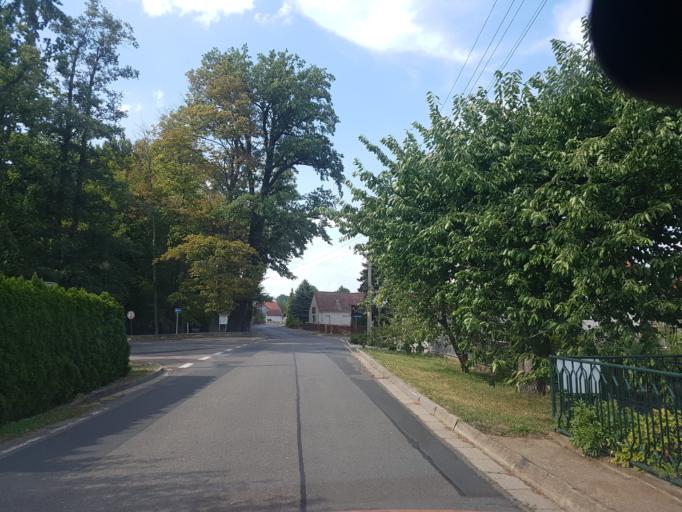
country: DE
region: Saxony
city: Stauchitz
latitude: 51.2377
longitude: 13.1929
